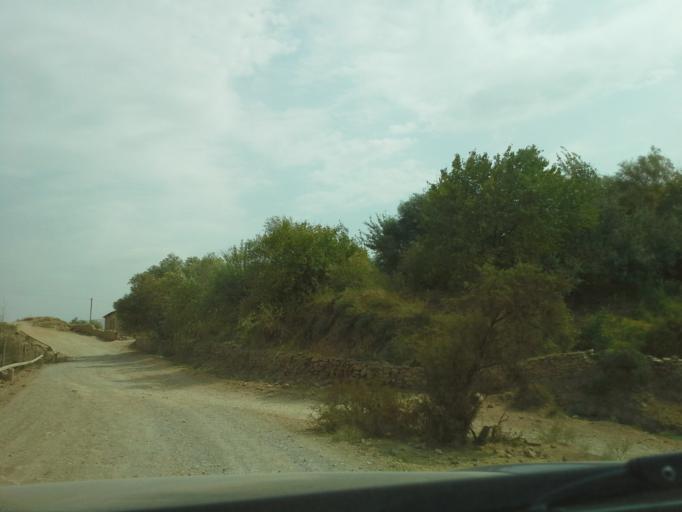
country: UZ
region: Qashqadaryo
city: Qorashina
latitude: 37.9335
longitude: 66.5084
